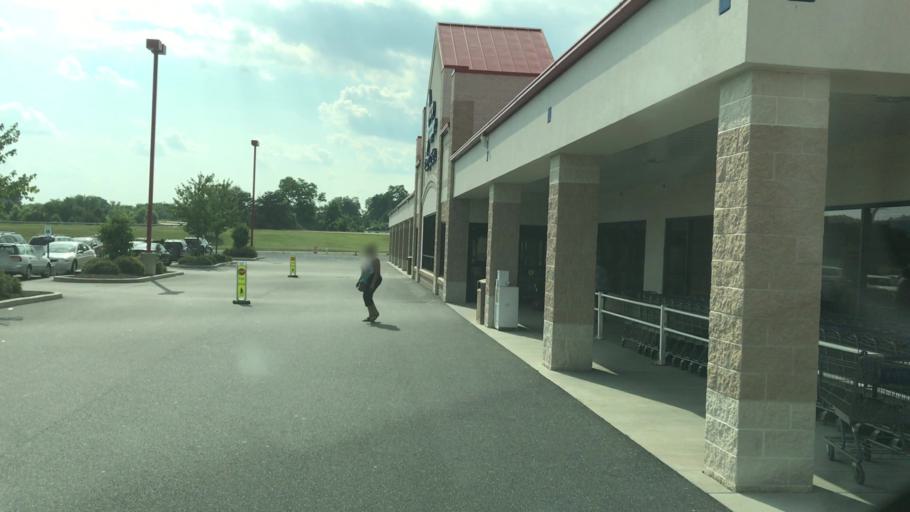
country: US
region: Pennsylvania
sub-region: Dauphin County
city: Middletown
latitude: 40.2016
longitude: -76.7557
